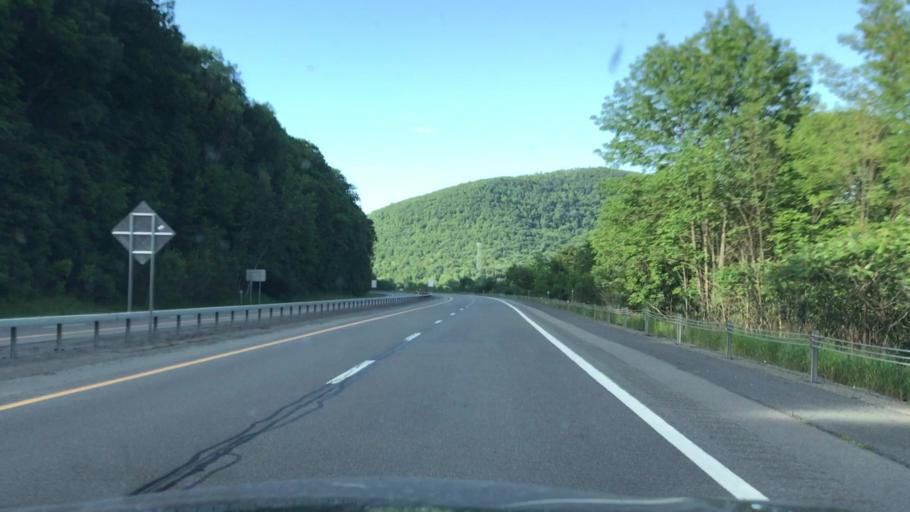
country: US
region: New York
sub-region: Delaware County
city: Hancock
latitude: 41.9572
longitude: -75.2686
